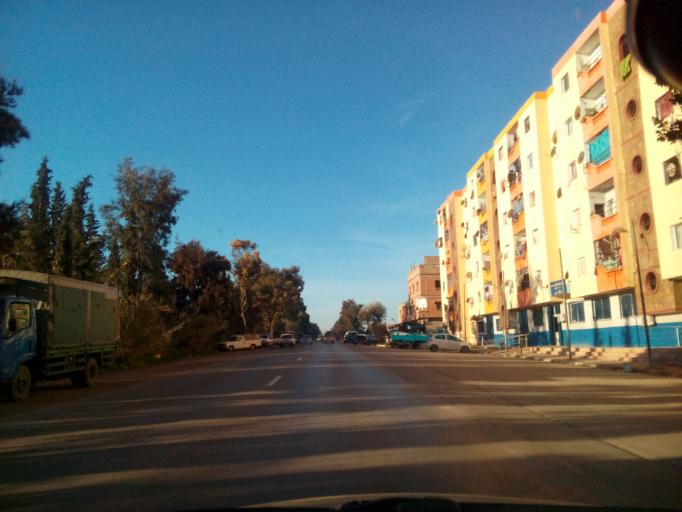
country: DZ
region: Relizane
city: Relizane
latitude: 35.7184
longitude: 0.3576
